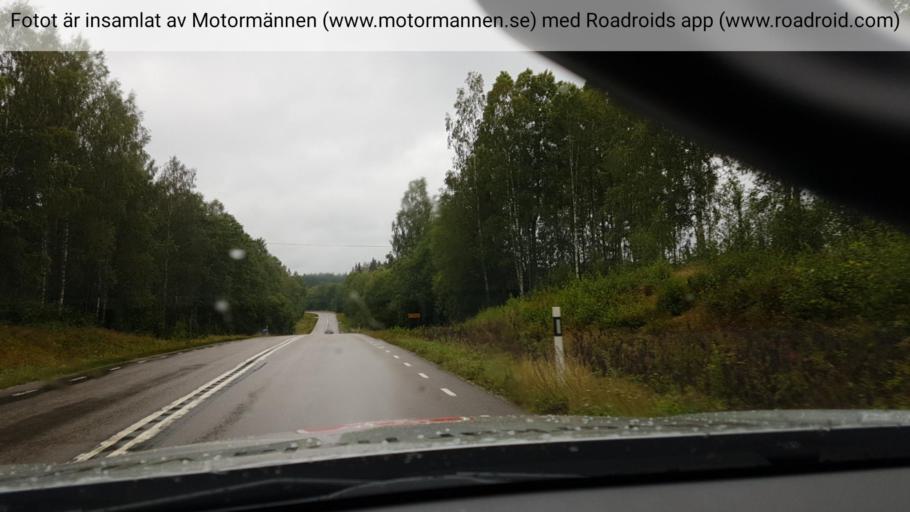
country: SE
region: Vaestra Goetaland
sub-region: Bengtsfors Kommun
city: Billingsfors
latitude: 58.9402
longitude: 12.1173
